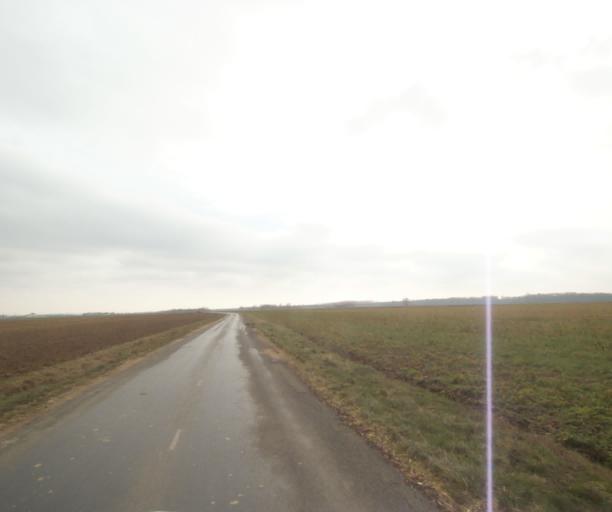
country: FR
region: Champagne-Ardenne
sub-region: Departement de la Haute-Marne
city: Villiers-en-Lieu
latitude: 48.6798
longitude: 4.8497
